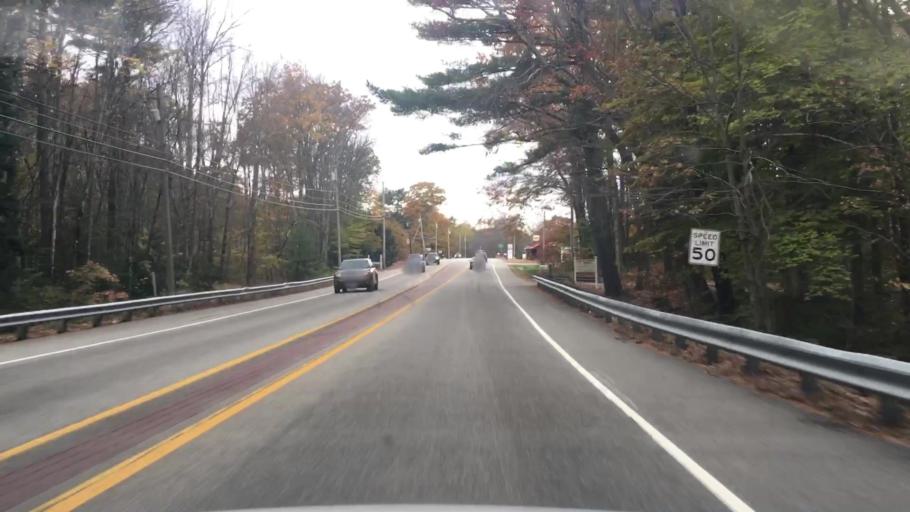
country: US
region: Maine
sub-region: York County
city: West Kennebunk
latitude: 43.4784
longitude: -70.5842
